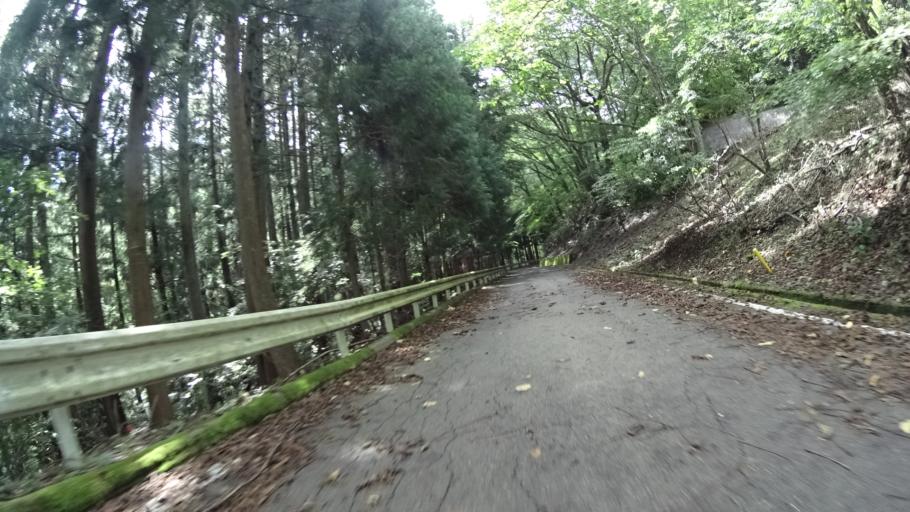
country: JP
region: Yamanashi
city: Enzan
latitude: 35.6107
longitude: 138.7903
